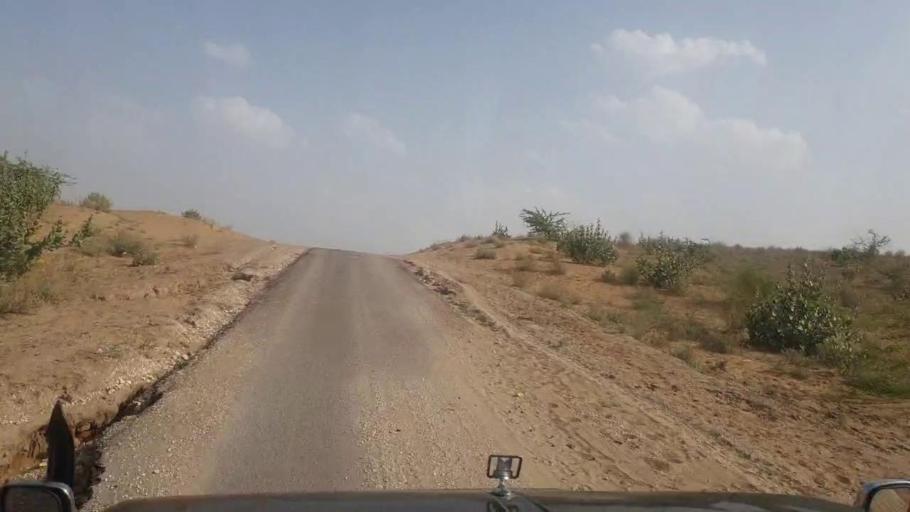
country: PK
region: Sindh
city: Islamkot
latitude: 25.1385
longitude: 70.3190
